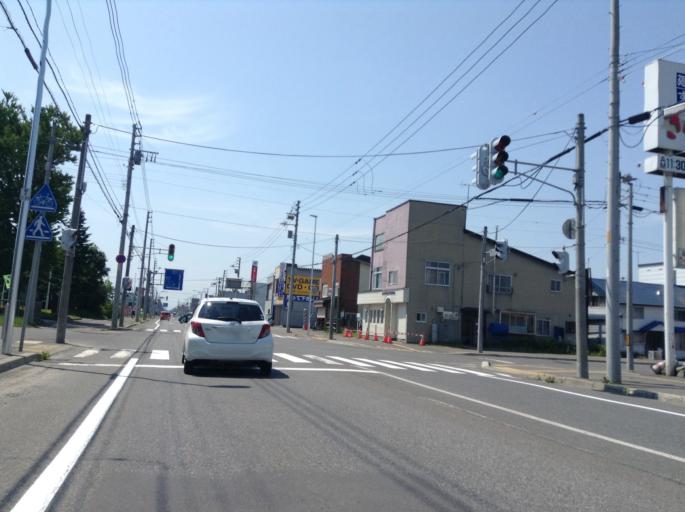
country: JP
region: Hokkaido
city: Nayoro
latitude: 44.3581
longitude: 142.4572
